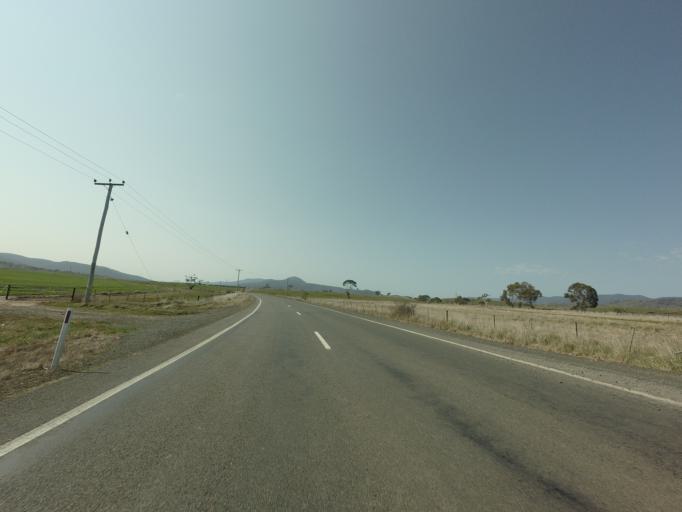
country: AU
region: Tasmania
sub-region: Northern Midlands
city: Evandale
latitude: -41.8096
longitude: 147.6704
